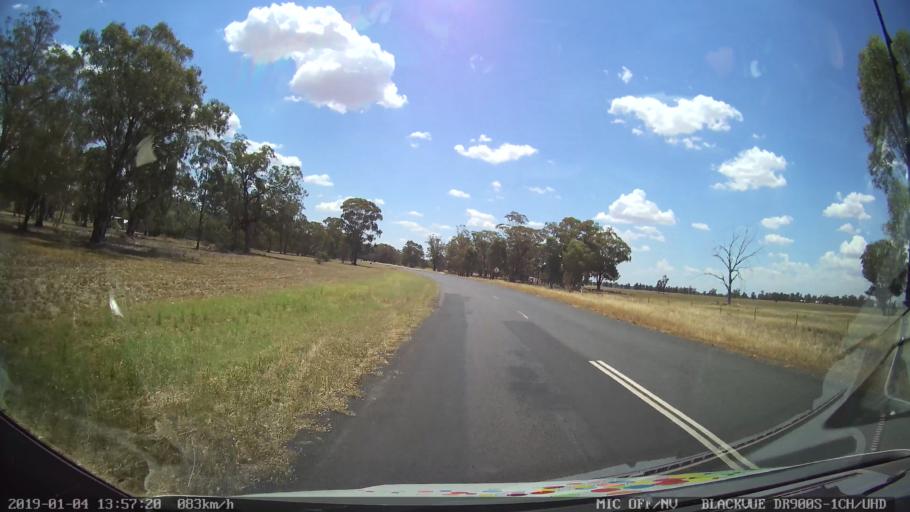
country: AU
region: New South Wales
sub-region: Dubbo Municipality
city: Dubbo
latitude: -32.3413
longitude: 148.6002
